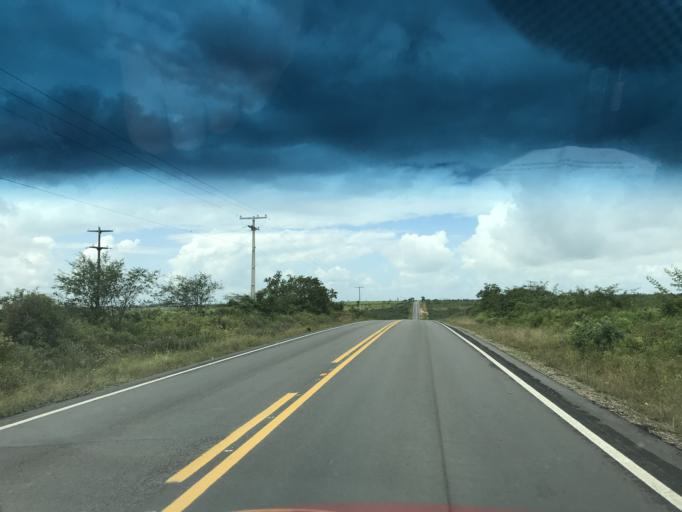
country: BR
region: Bahia
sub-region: Conceicao Do Almeida
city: Conceicao do Almeida
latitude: -12.6725
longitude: -39.2707
